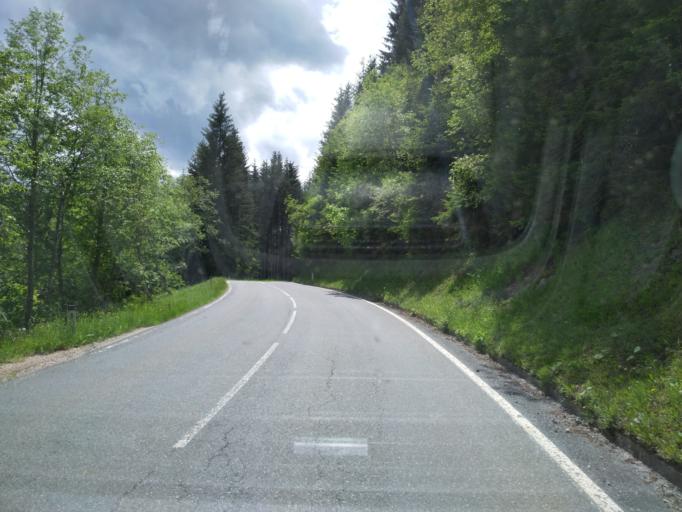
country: AT
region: Salzburg
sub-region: Politischer Bezirk Sankt Johann im Pongau
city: Filzmoos
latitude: 47.4417
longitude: 13.5773
